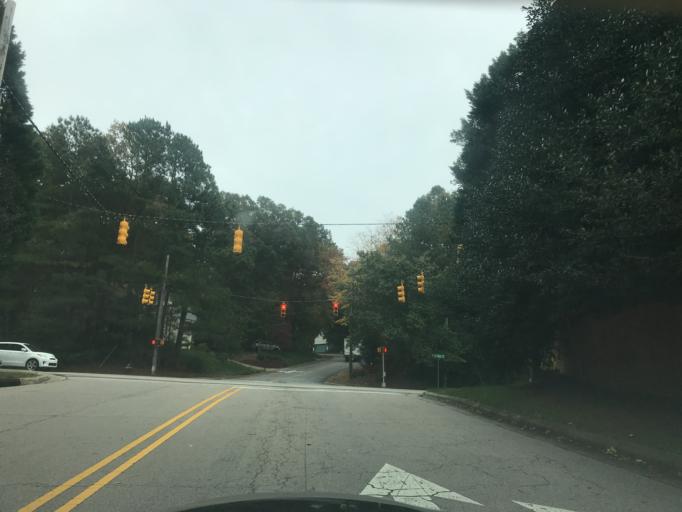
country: US
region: North Carolina
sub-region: Wake County
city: West Raleigh
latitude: 35.8943
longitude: -78.6640
